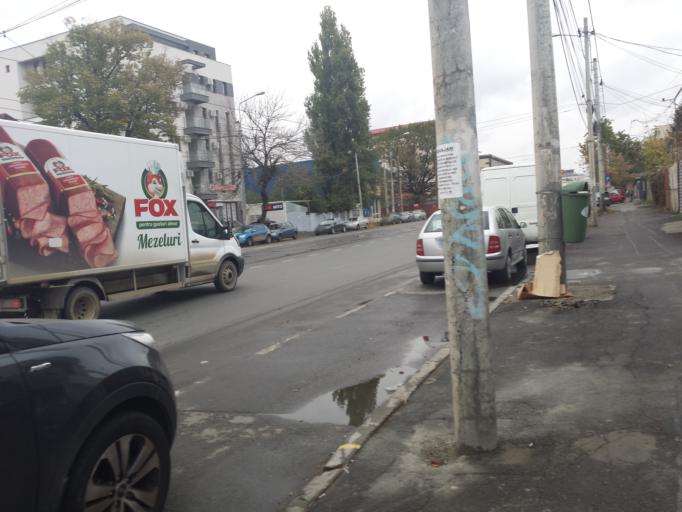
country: RO
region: Ilfov
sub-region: Comuna Chiajna
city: Rosu
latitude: 44.4834
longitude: 26.0266
